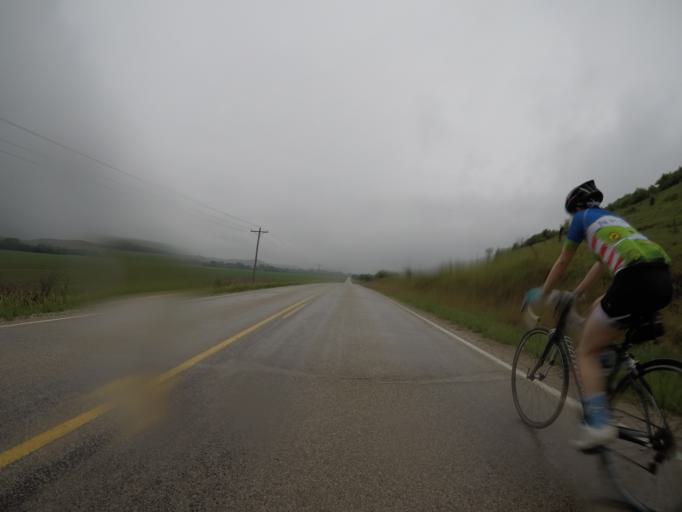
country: US
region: Kansas
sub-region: Pottawatomie County
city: Wamego
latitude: 39.3938
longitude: -96.1895
